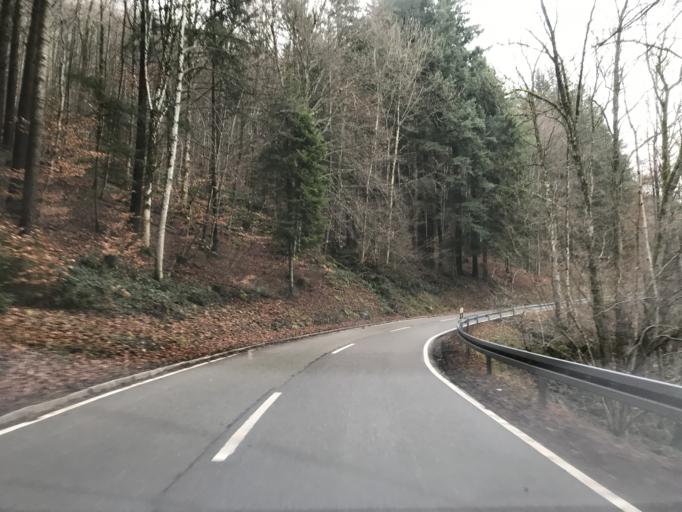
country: DE
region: Baden-Wuerttemberg
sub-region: Freiburg Region
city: Wehr
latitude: 47.6157
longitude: 7.9355
